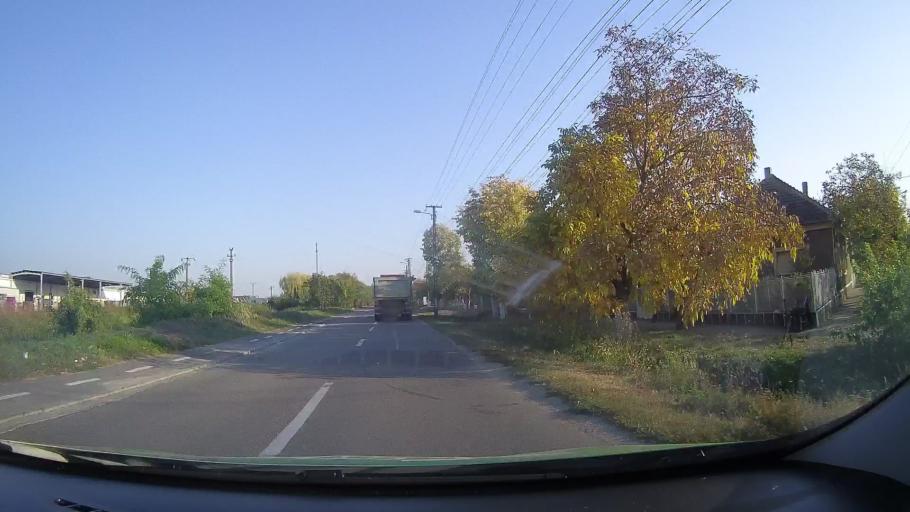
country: RO
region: Arad
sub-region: Comuna Pancota
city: Pancota
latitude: 46.3207
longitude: 21.6923
